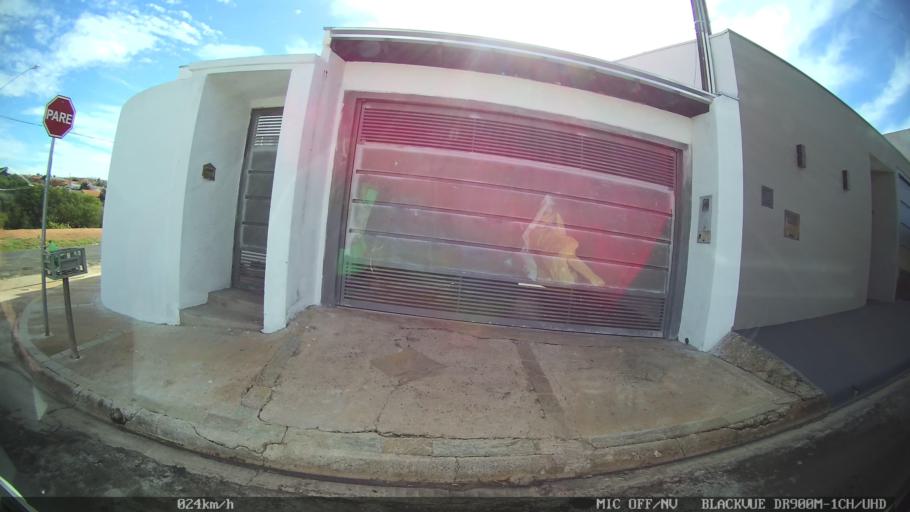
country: BR
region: Sao Paulo
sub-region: Catanduva
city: Catanduva
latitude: -21.1275
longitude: -48.9424
